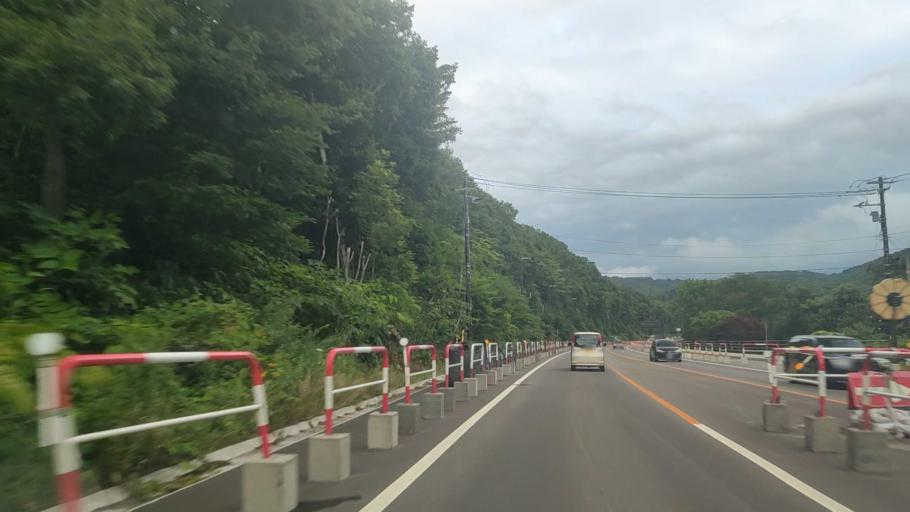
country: JP
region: Hokkaido
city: Nanae
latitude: 41.9876
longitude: 140.6394
